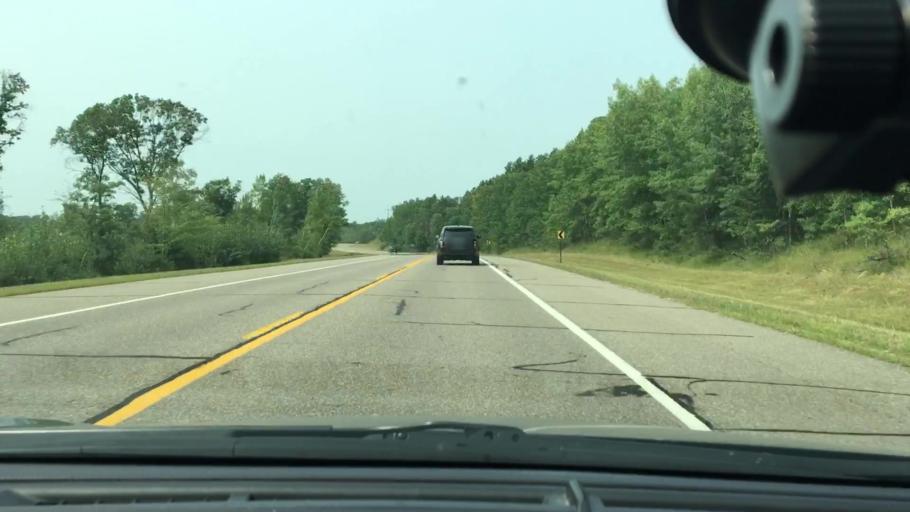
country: US
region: Minnesota
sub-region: Cass County
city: East Gull Lake
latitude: 46.3838
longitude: -94.3188
